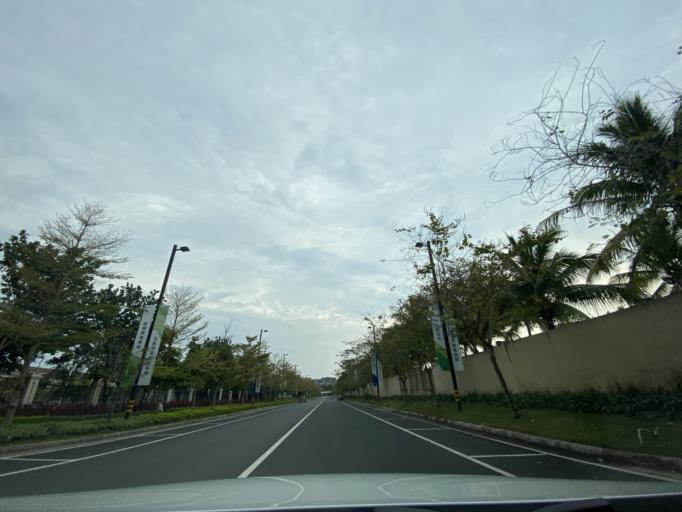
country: CN
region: Hainan
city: Yingzhou
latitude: 18.4043
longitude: 109.8543
